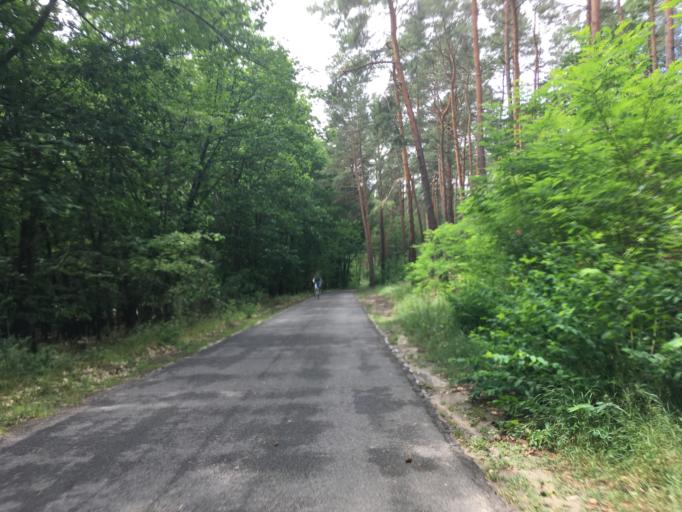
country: DE
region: Berlin
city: Muggelheim
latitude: 52.4053
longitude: 13.6522
